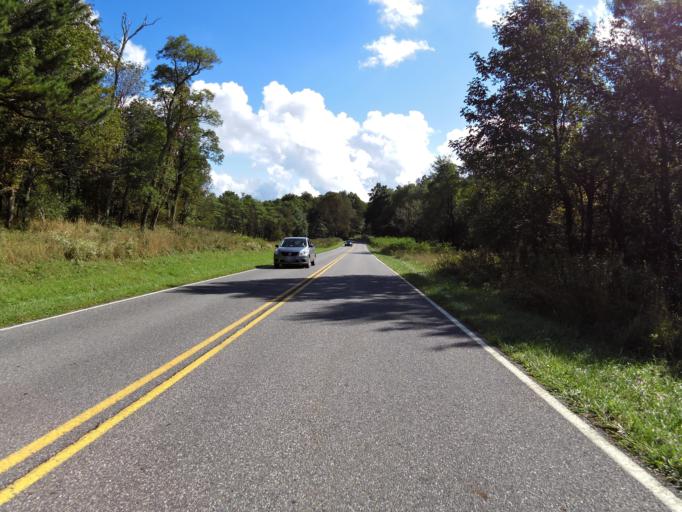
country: US
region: Virginia
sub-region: Page County
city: Stanley
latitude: 38.5462
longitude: -78.4150
